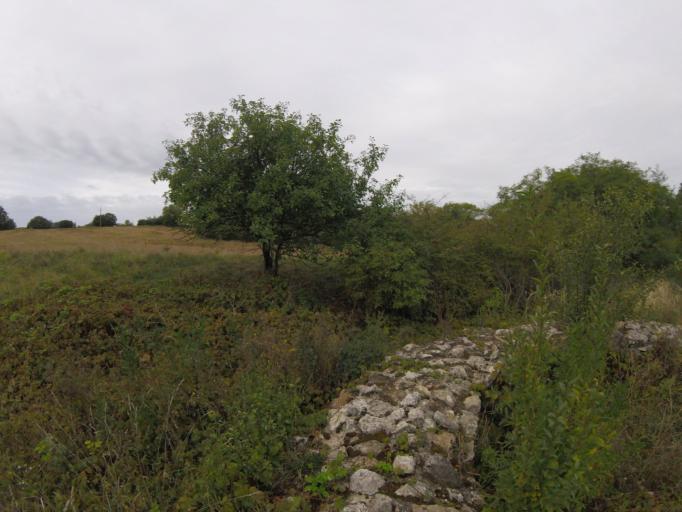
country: HU
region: Komarom-Esztergom
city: Tokod
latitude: 47.7268
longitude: 18.6760
